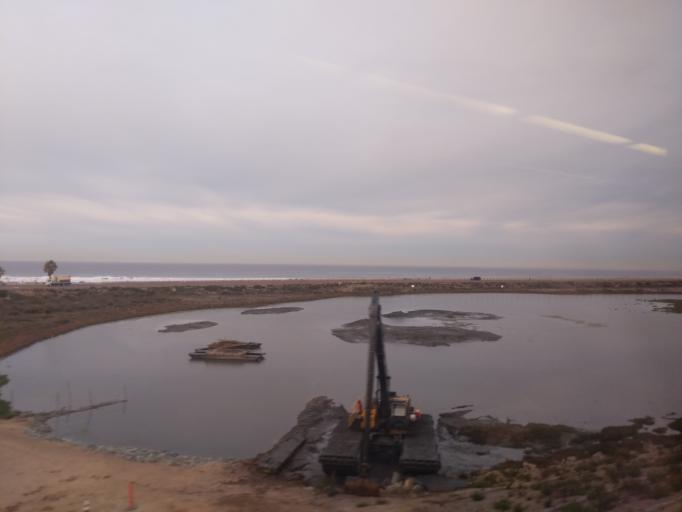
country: US
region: California
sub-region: San Diego County
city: Solana Beach
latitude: 33.0033
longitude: -117.2756
